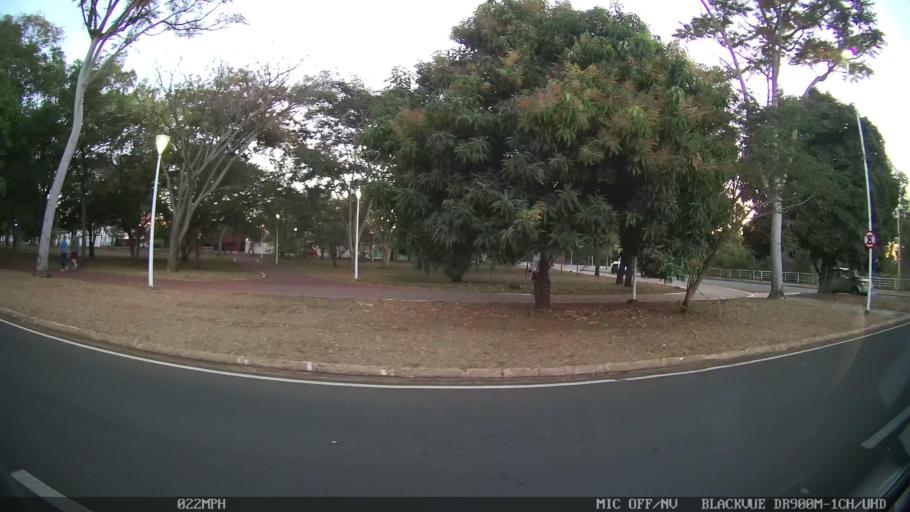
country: BR
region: Sao Paulo
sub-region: Sao Jose Do Rio Preto
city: Sao Jose do Rio Preto
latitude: -20.8460
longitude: -49.3935
